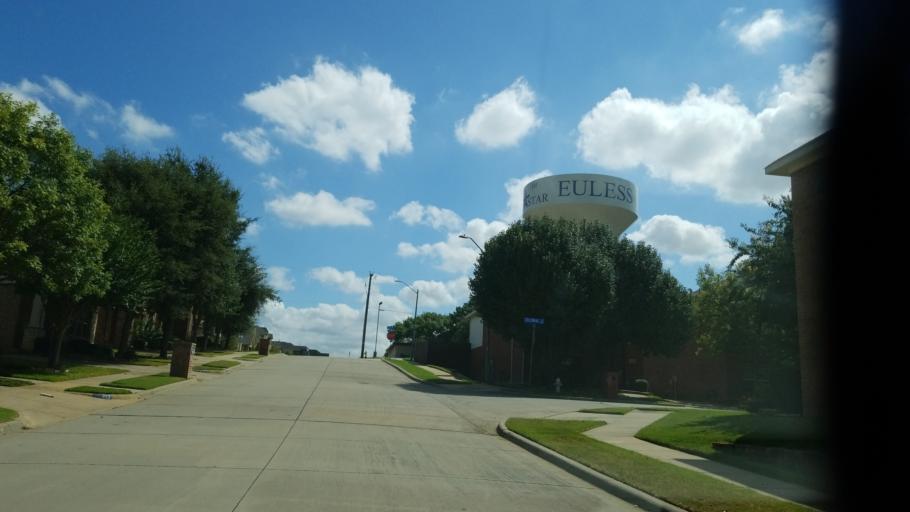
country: US
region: Texas
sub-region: Tarrant County
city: Euless
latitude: 32.8358
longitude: -97.0804
